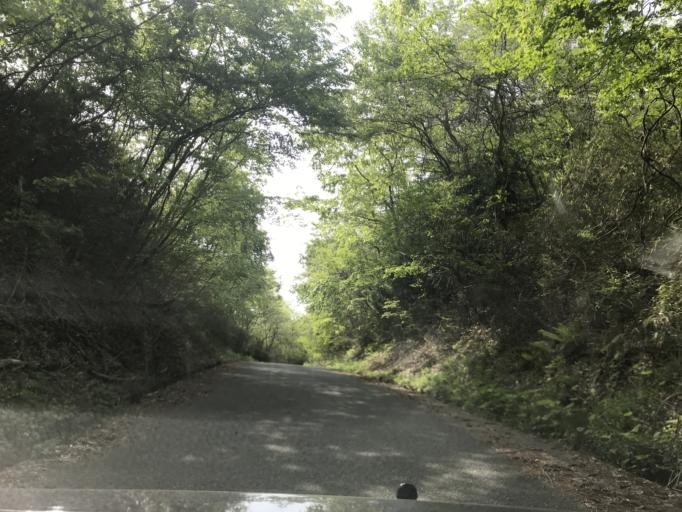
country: JP
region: Iwate
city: Ichinoseki
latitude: 38.8891
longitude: 141.0584
